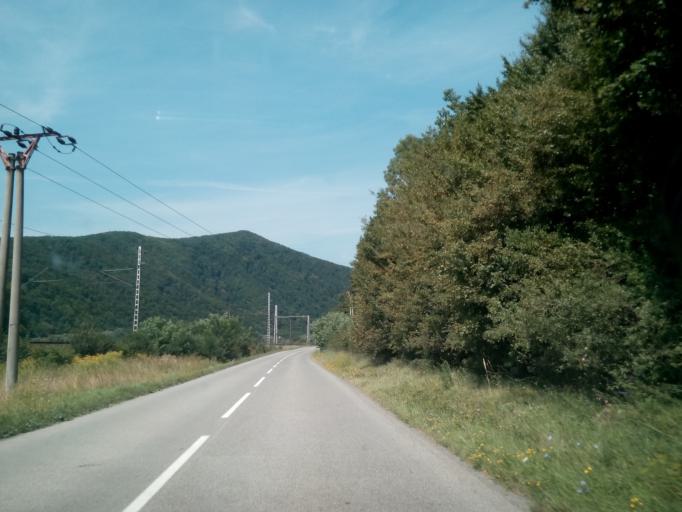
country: SK
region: Kosicky
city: Kosice
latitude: 48.8260
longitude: 21.2265
